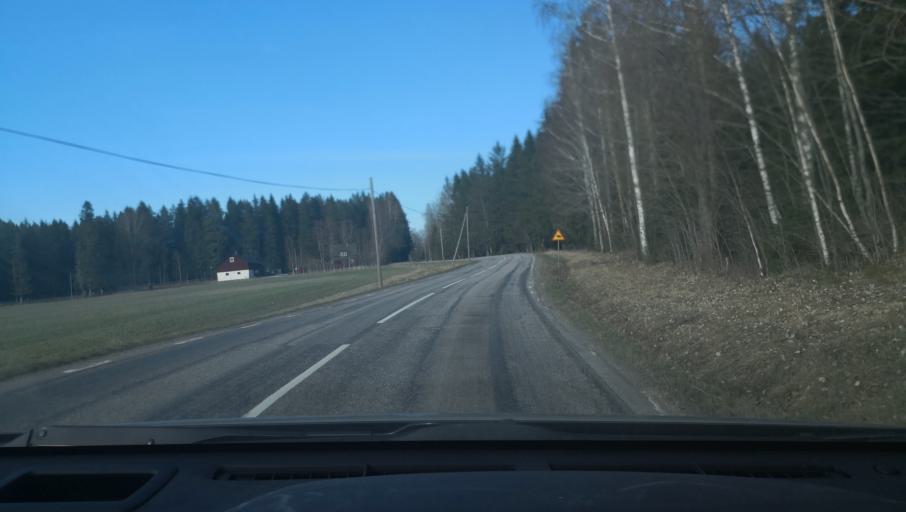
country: SE
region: Uppsala
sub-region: Heby Kommun
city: Heby
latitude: 59.9706
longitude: 16.8959
